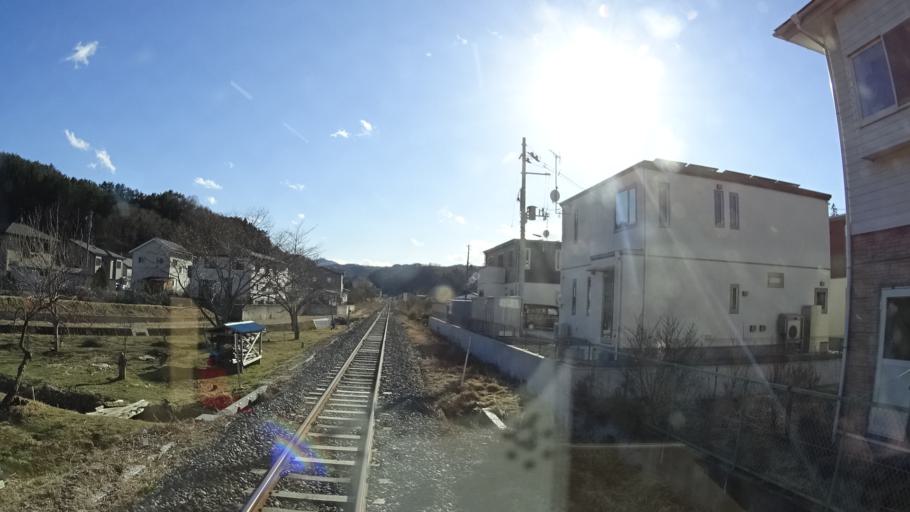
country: JP
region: Iwate
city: Miyako
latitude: 39.6186
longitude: 141.9455
